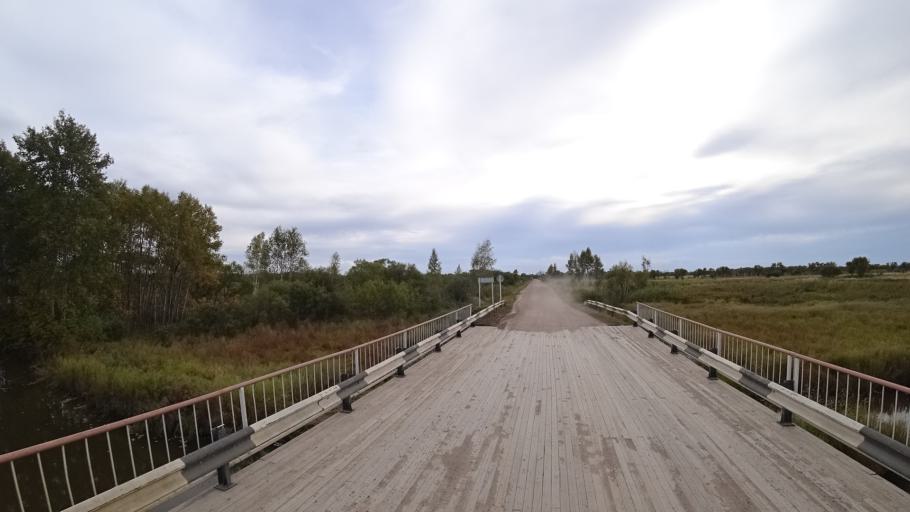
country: RU
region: Amur
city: Arkhara
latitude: 49.3784
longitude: 130.2127
